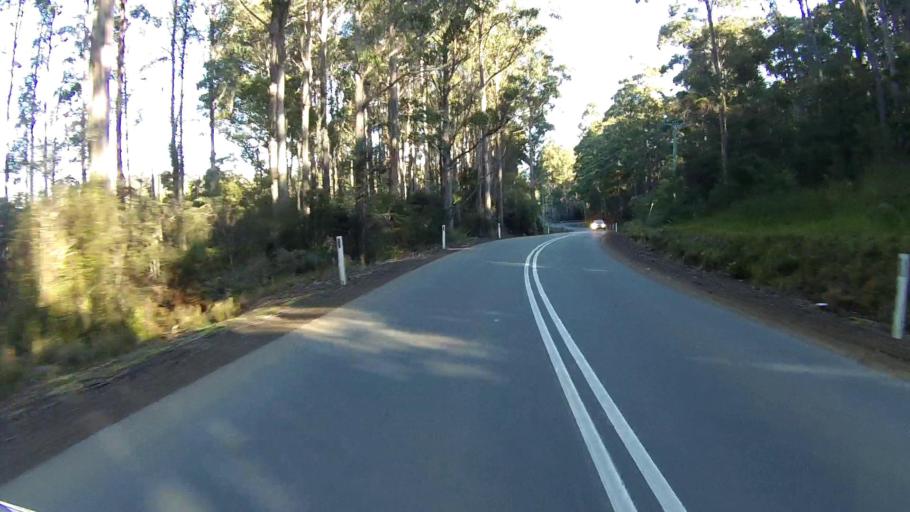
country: AU
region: Tasmania
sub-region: Clarence
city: Sandford
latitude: -43.0960
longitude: 147.8711
